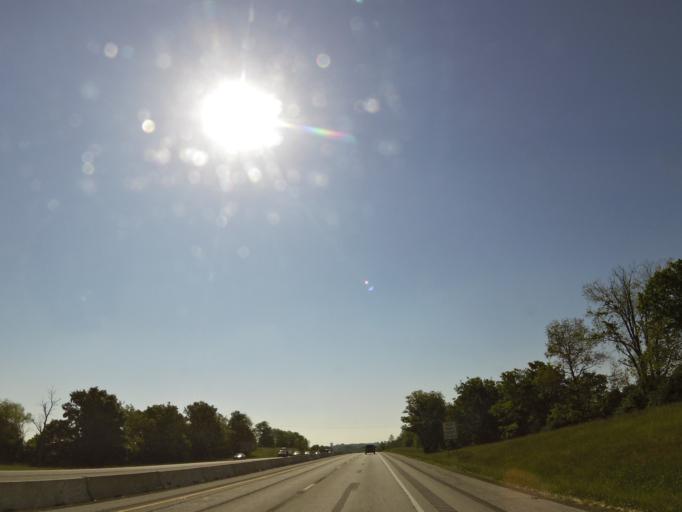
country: US
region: Kentucky
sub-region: Shelby County
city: Shelbyville
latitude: 38.1886
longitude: -85.2591
